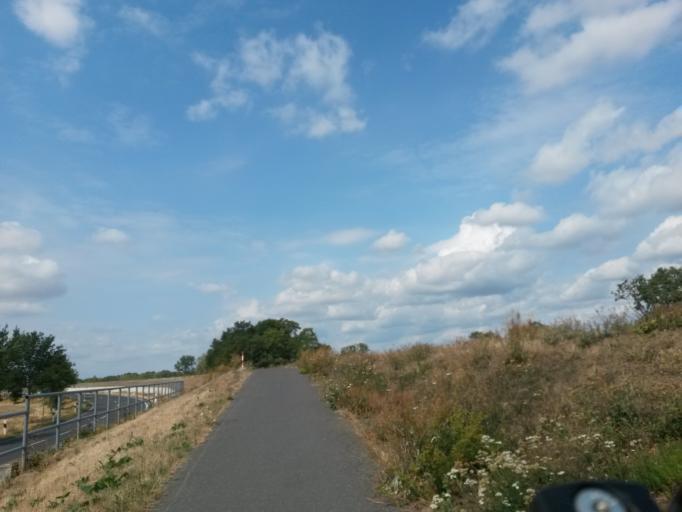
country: DE
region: Saxony-Anhalt
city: Abtsdorf
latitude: 51.8414
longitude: 12.6879
